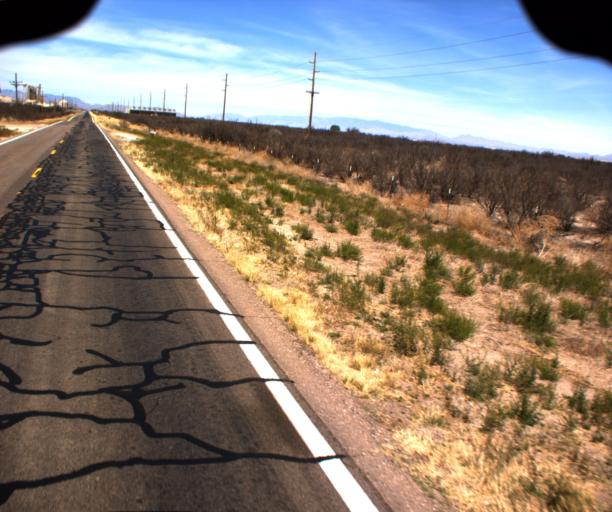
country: US
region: Arizona
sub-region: Cochise County
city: Willcox
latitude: 32.0498
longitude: -109.8859
